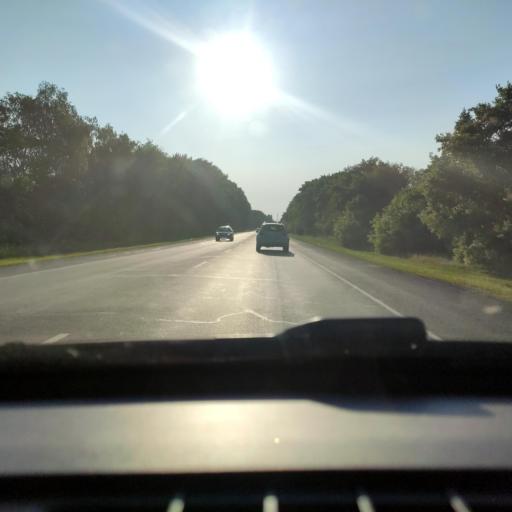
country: RU
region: Voronezj
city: Kashirskoye
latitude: 51.4923
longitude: 39.6108
